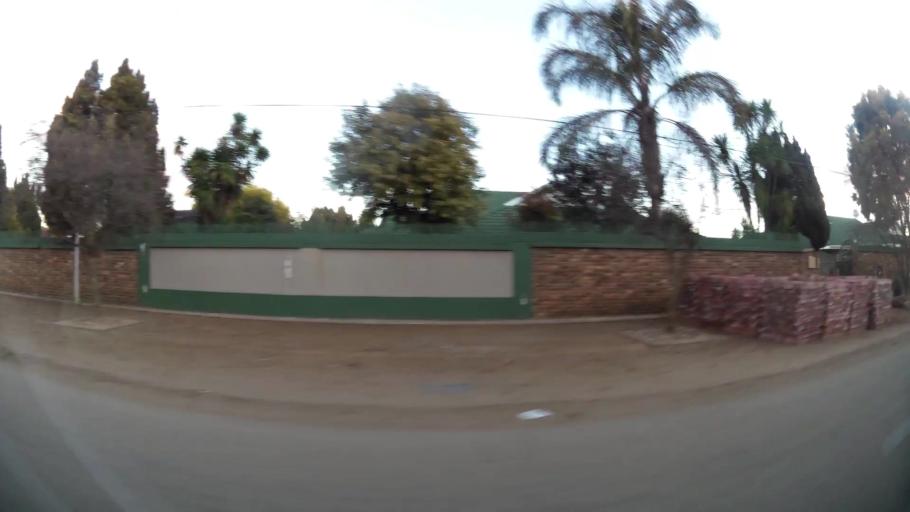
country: ZA
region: North-West
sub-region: Dr Kenneth Kaunda District Municipality
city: Potchefstroom
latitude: -26.7222
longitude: 27.1188
